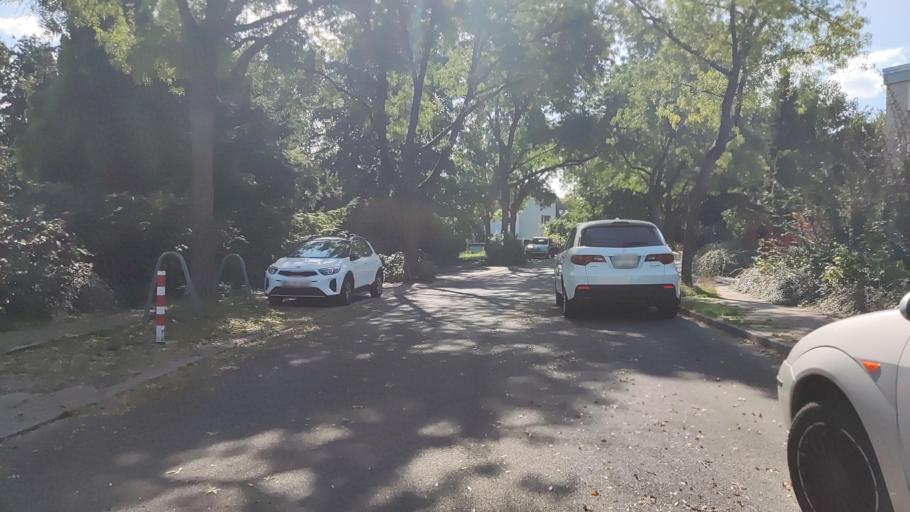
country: DE
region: North Rhine-Westphalia
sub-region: Regierungsbezirk Arnsberg
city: Bochum
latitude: 51.4609
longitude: 7.2530
